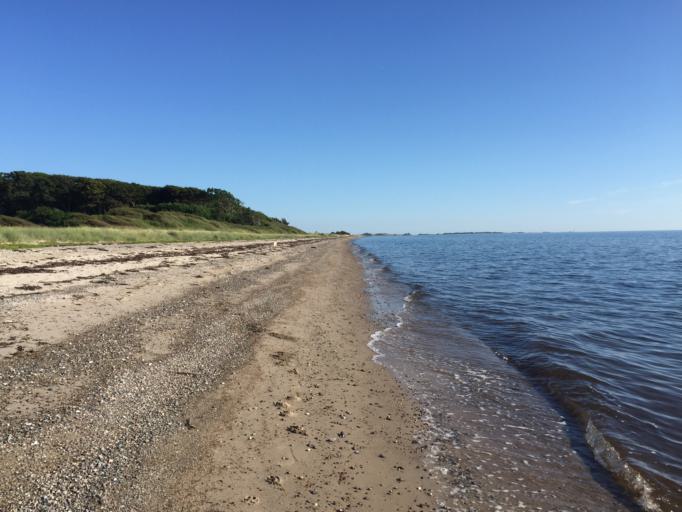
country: DK
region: Zealand
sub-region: Slagelse Kommune
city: Korsor
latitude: 55.2256
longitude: 11.1717
